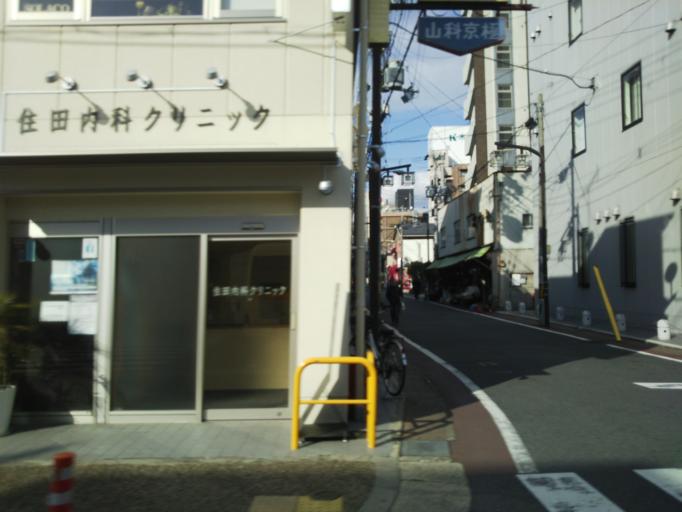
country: JP
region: Shiga Prefecture
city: Otsu-shi
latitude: 34.9889
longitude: 135.8131
